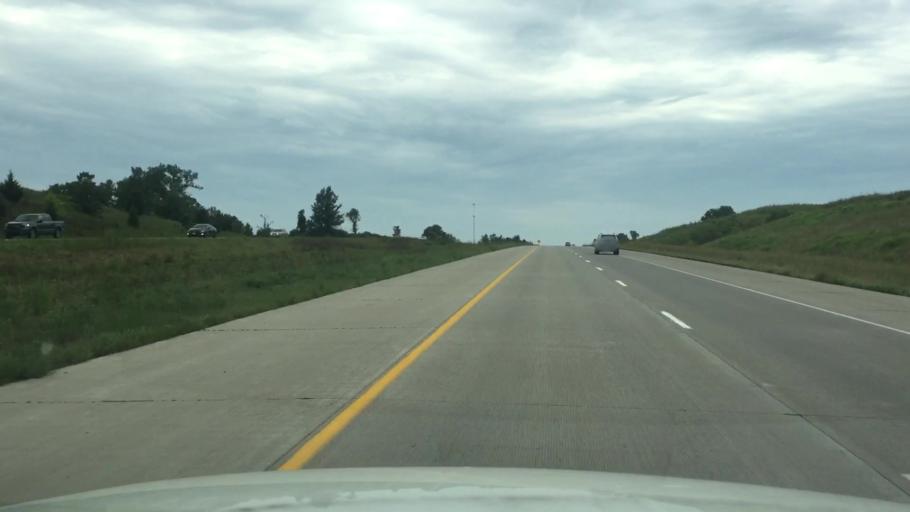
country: US
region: Iowa
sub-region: Warren County
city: Norwalk
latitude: 41.4530
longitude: -93.7801
